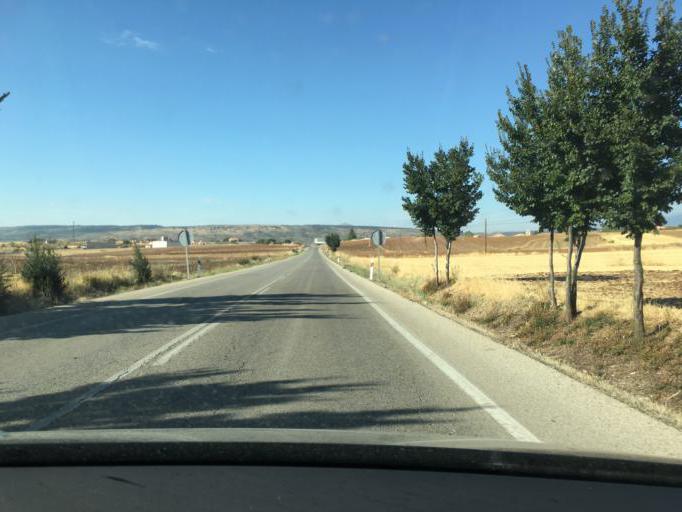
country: ES
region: Madrid
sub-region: Provincia de Madrid
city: Torrelaguna
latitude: 40.8318
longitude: -3.5235
